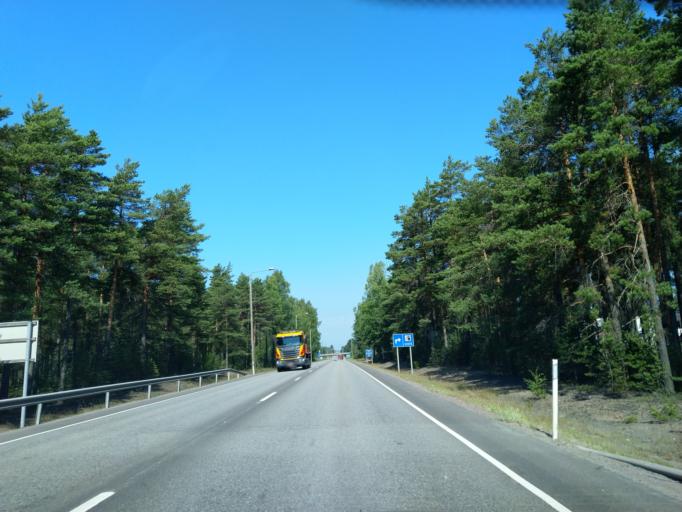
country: FI
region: Satakunta
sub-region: Pori
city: Harjavalta
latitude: 61.3030
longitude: 22.1376
